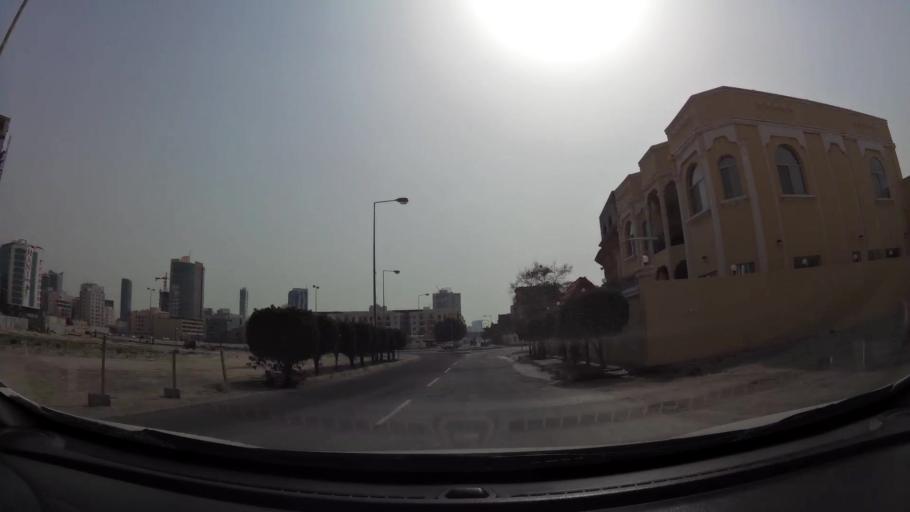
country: BH
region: Manama
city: Jidd Hafs
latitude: 26.2350
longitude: 50.5276
